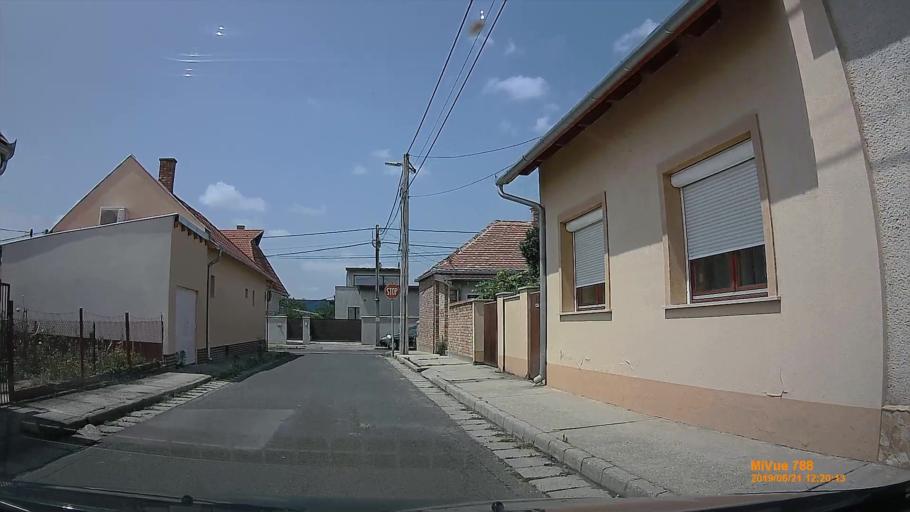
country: HU
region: Baranya
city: Pellerd
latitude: 46.0634
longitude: 18.1878
